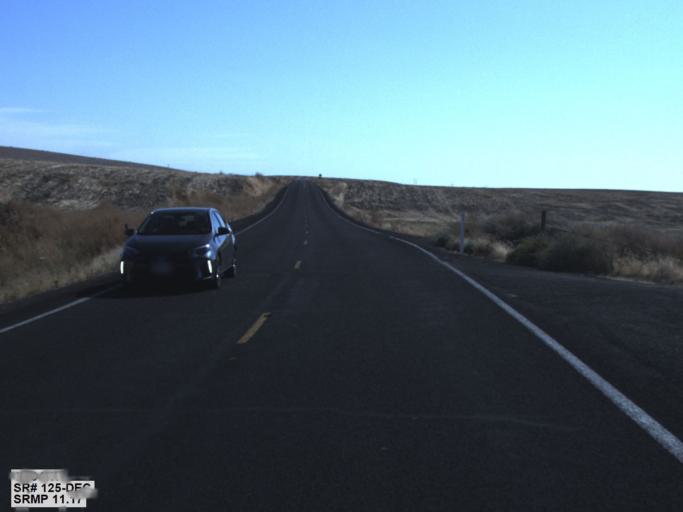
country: US
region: Washington
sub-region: Walla Walla County
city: Walla Walla
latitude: 46.1340
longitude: -118.3760
